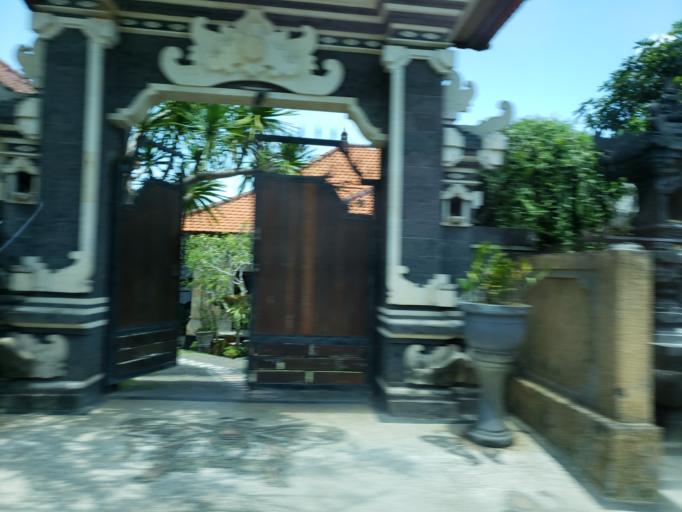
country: ID
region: Bali
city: Kangin
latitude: -8.8398
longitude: 115.1392
